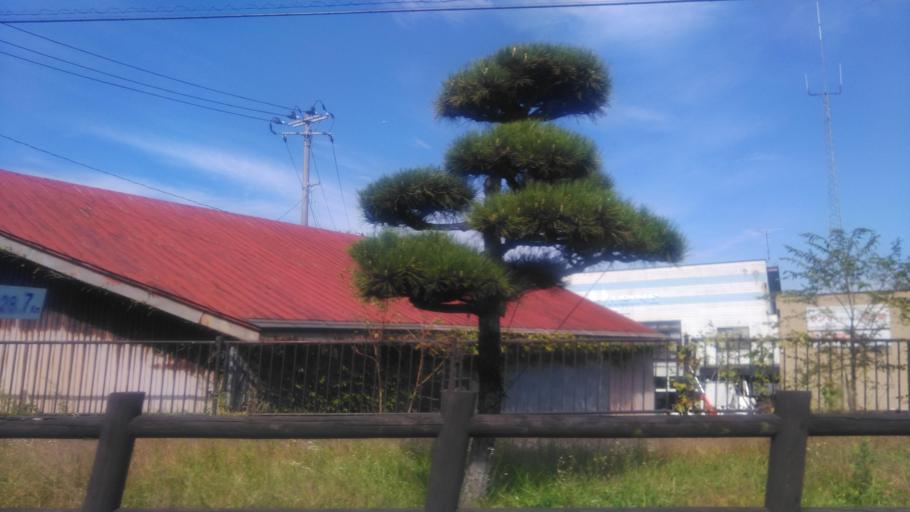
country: JP
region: Akita
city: Noshiromachi
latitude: 40.1903
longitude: 140.0160
